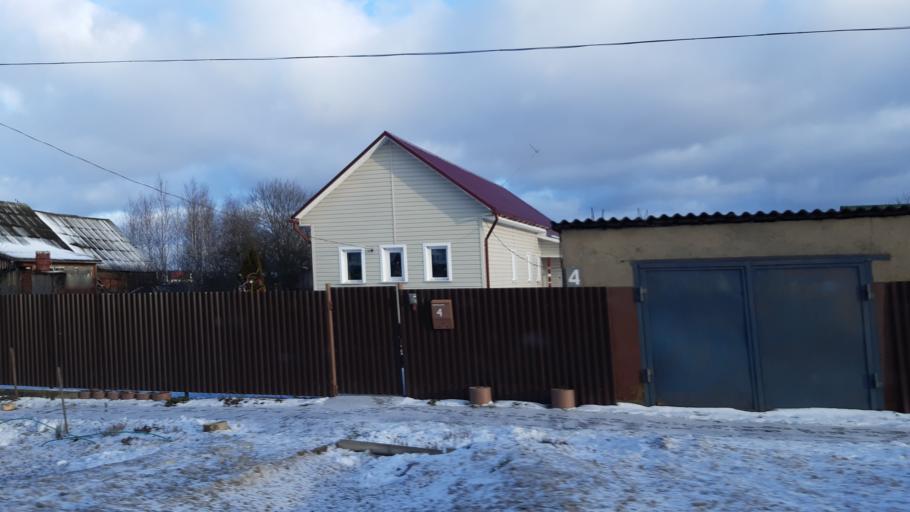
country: RU
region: Moskovskaya
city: Noginsk-9
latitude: 56.0496
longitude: 38.5513
